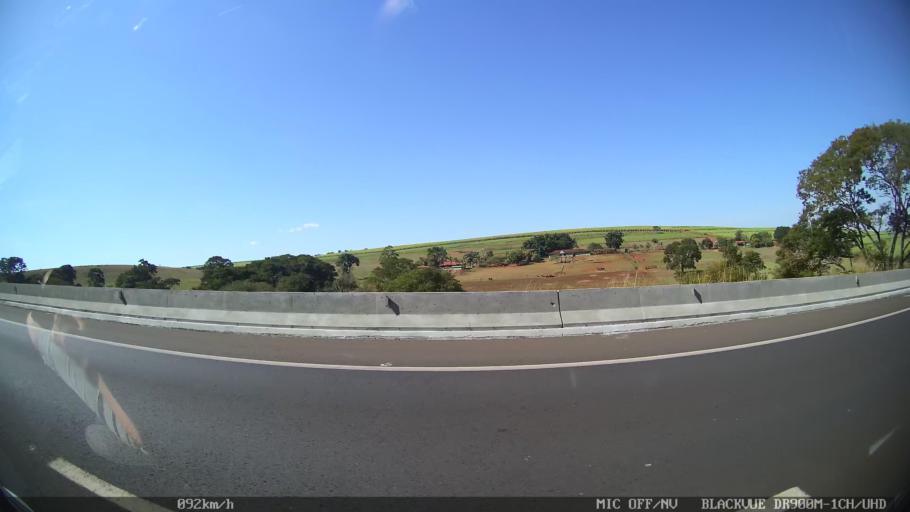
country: BR
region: Sao Paulo
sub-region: Franca
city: Franca
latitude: -20.7008
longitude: -47.5011
